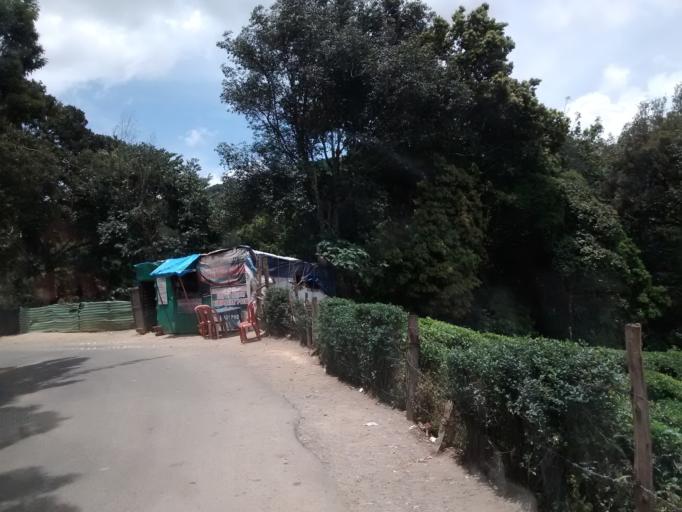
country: IN
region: Tamil Nadu
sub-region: Theni
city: Bodinayakkanur
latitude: 10.1278
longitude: 77.2371
